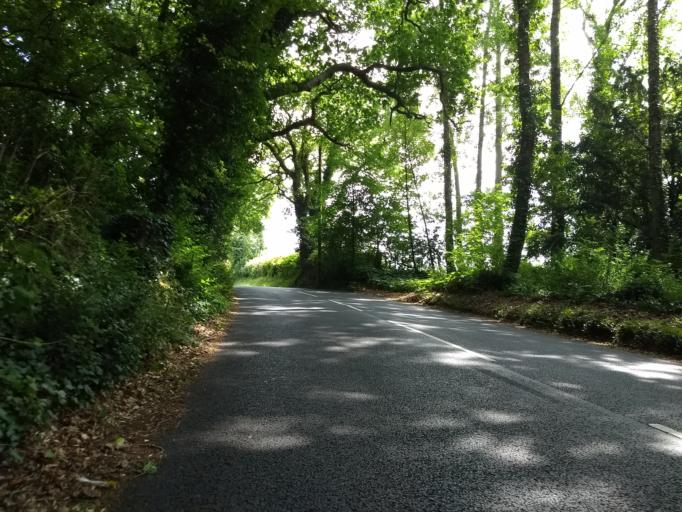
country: GB
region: England
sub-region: Isle of Wight
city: Seaview
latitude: 50.7139
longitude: -1.1378
